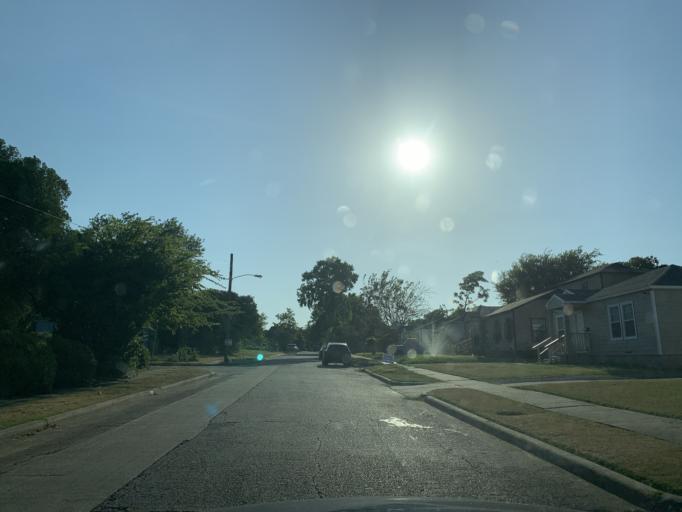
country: US
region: Texas
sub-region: Dallas County
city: Dallas
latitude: 32.7125
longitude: -96.7896
